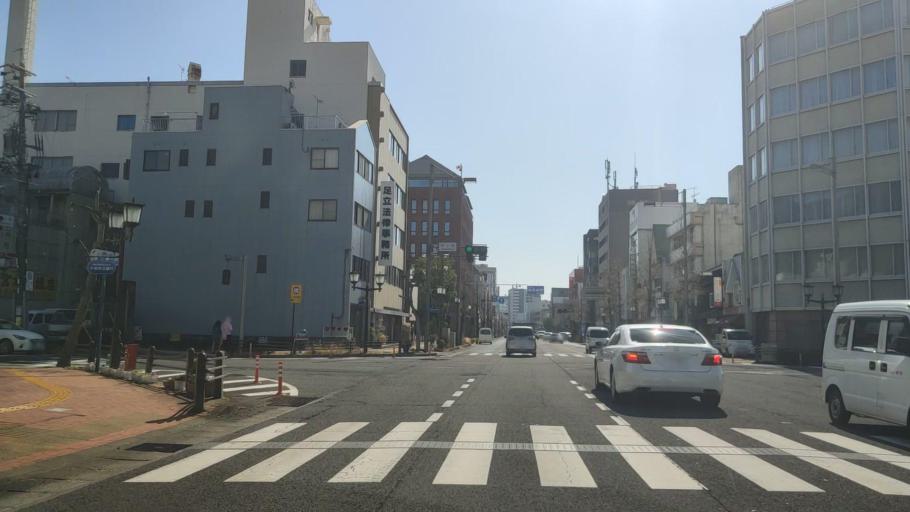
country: JP
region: Gifu
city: Gifu-shi
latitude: 35.4253
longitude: 136.7622
